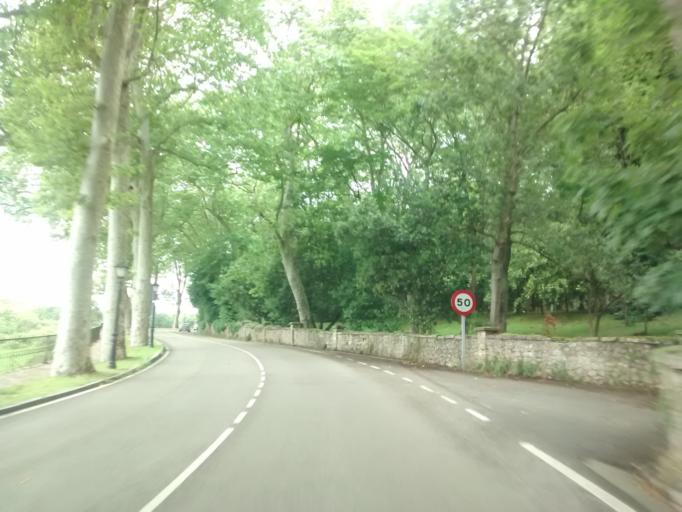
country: ES
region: Cantabria
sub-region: Provincia de Cantabria
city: Santillana
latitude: 43.3898
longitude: -4.1101
